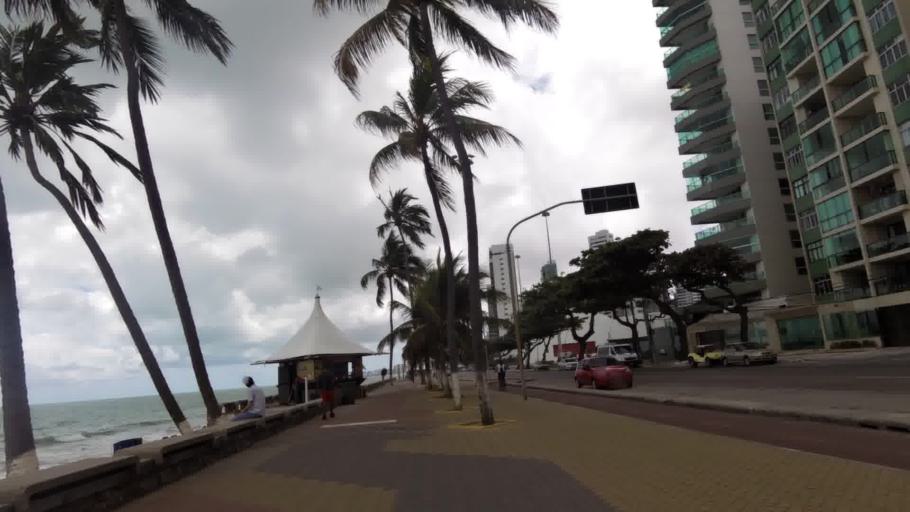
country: BR
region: Pernambuco
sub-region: Recife
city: Recife
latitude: -8.1400
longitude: -34.9028
